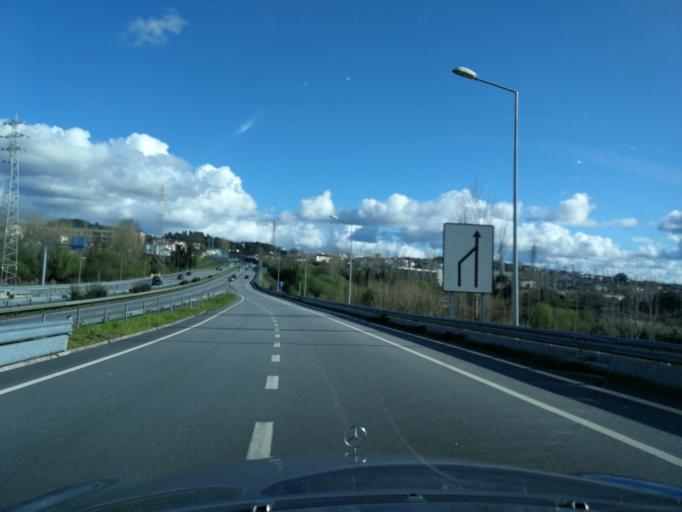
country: PT
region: Braga
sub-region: Braga
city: Braga
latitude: 41.5772
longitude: -8.4335
